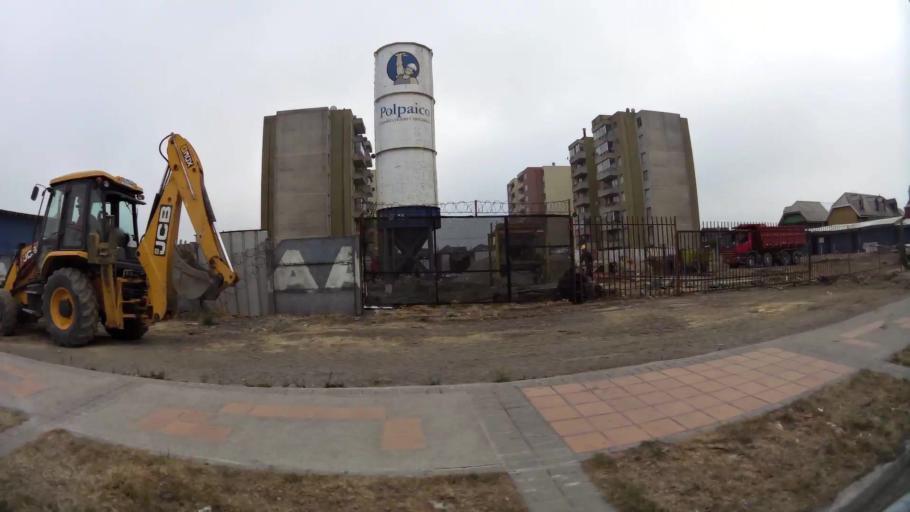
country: CL
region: Biobio
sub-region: Provincia de Concepcion
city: Concepcion
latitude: -36.7911
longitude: -73.0817
